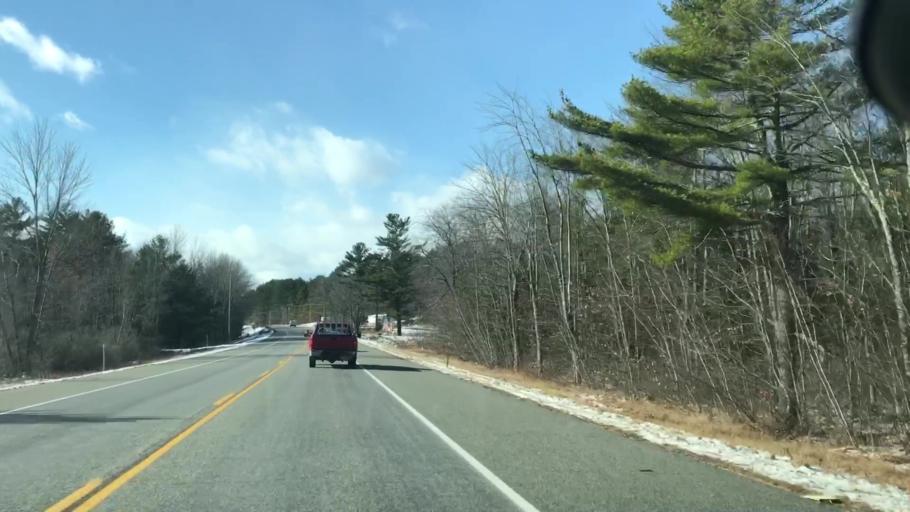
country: US
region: New Hampshire
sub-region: Carroll County
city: Freedom
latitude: 43.7889
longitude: -71.0861
